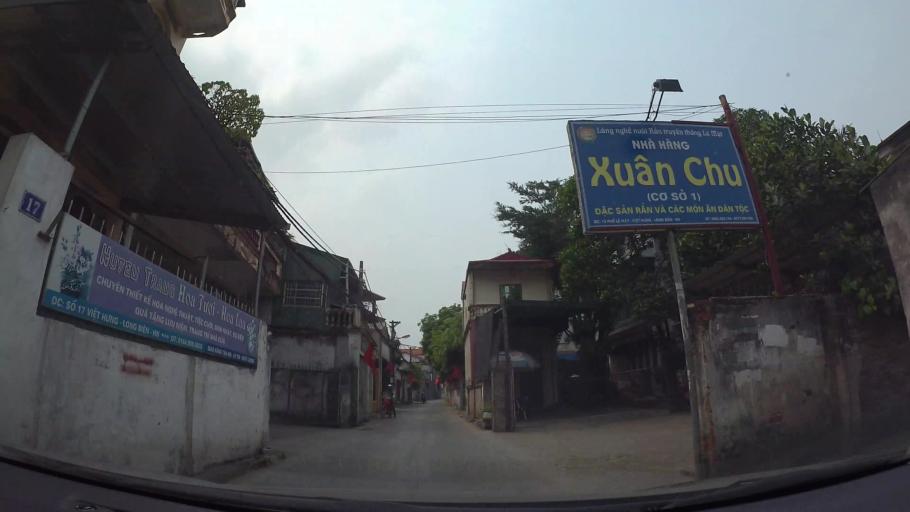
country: VN
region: Ha Noi
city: Trau Quy
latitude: 21.0546
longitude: 105.9001
